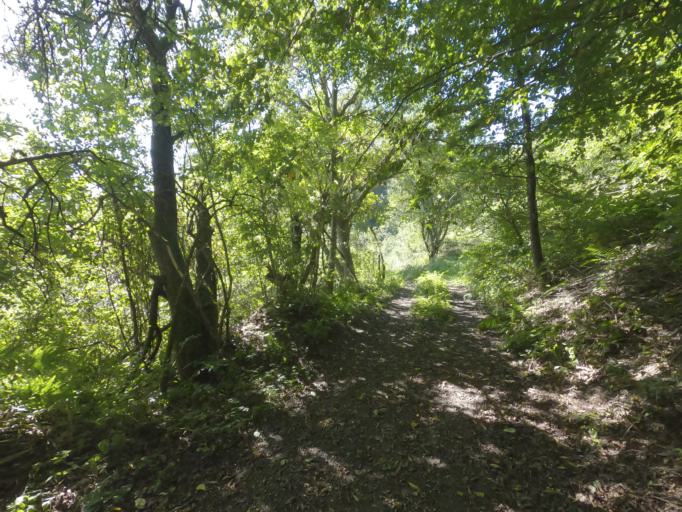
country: DE
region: Bavaria
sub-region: Lower Bavaria
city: Deggendorf
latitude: 48.8224
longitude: 13.0056
